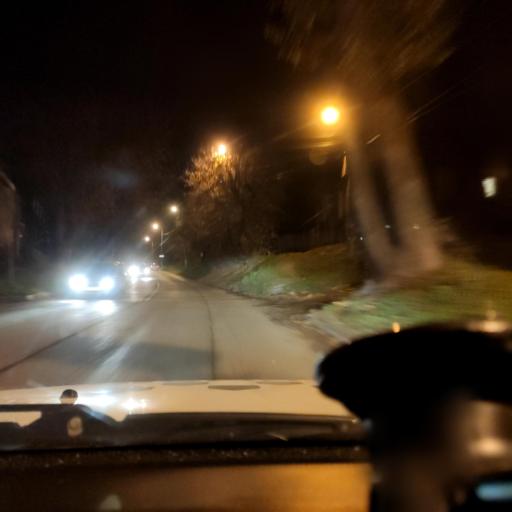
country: RU
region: Perm
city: Perm
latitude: 58.0364
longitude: 56.3188
